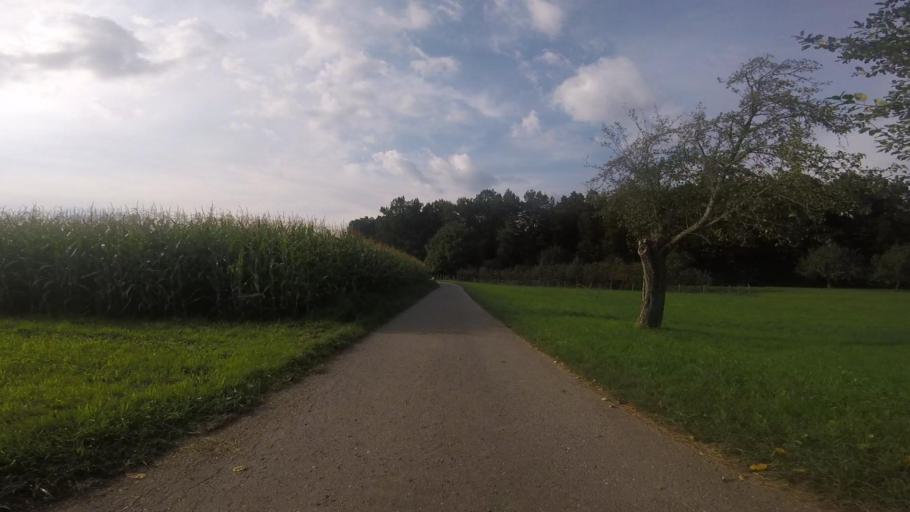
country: DE
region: Baden-Wuerttemberg
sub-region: Regierungsbezirk Stuttgart
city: Aspach
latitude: 48.9751
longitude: 9.3906
